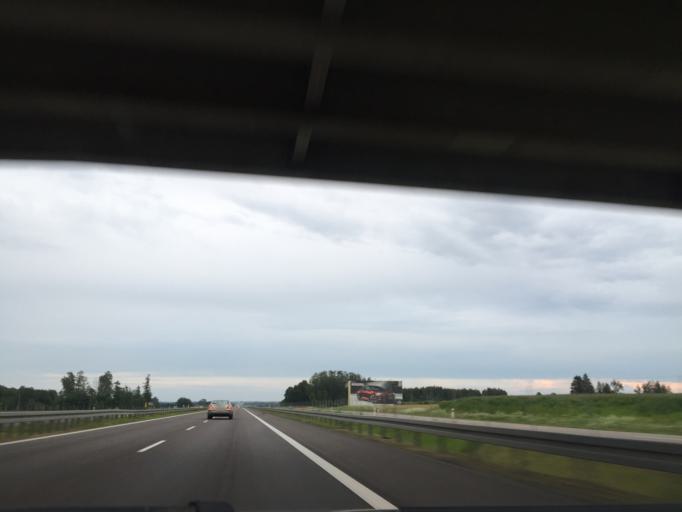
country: PL
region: Podlasie
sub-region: Powiat bialostocki
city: Tykocin
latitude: 53.1468
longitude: 22.8148
